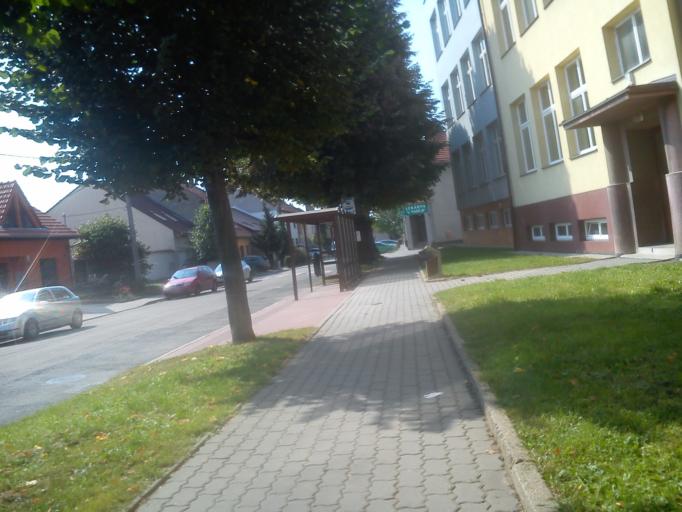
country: CZ
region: South Moravian
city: Sokolnice
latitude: 49.1041
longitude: 16.7540
